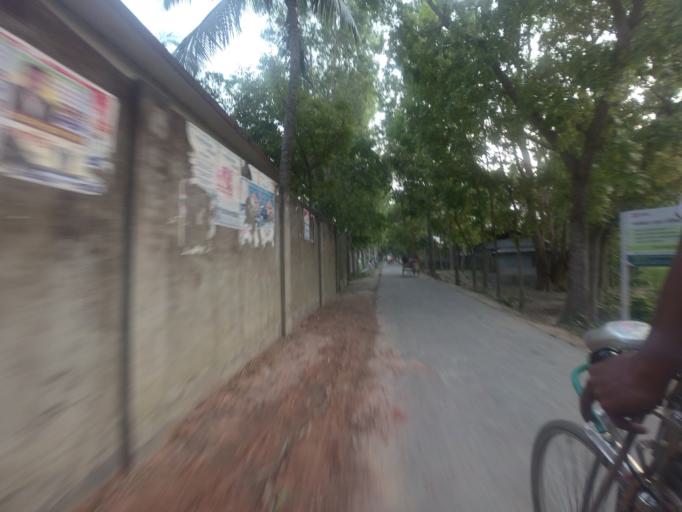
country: BD
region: Rajshahi
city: Sirajganj
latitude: 24.3252
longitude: 89.6759
